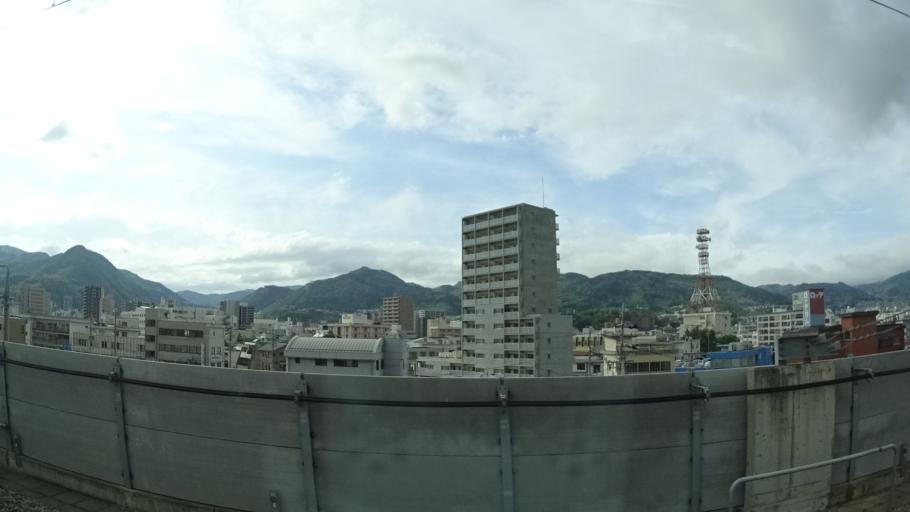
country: JP
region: Nagano
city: Nagano-shi
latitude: 36.6506
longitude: 138.1994
